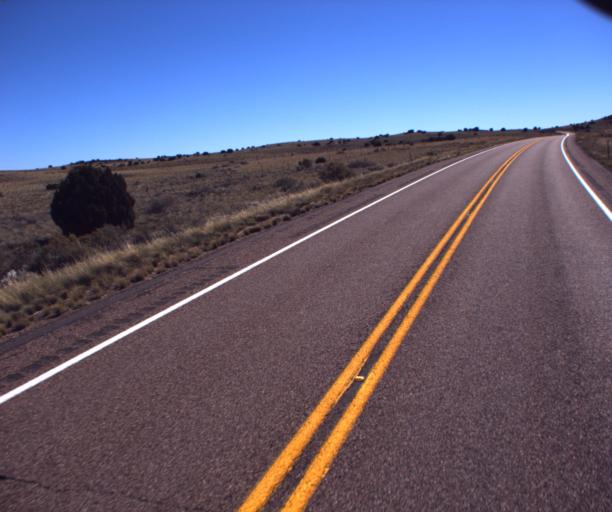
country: US
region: Arizona
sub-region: Apache County
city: Saint Johns
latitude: 34.5672
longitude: -109.5102
